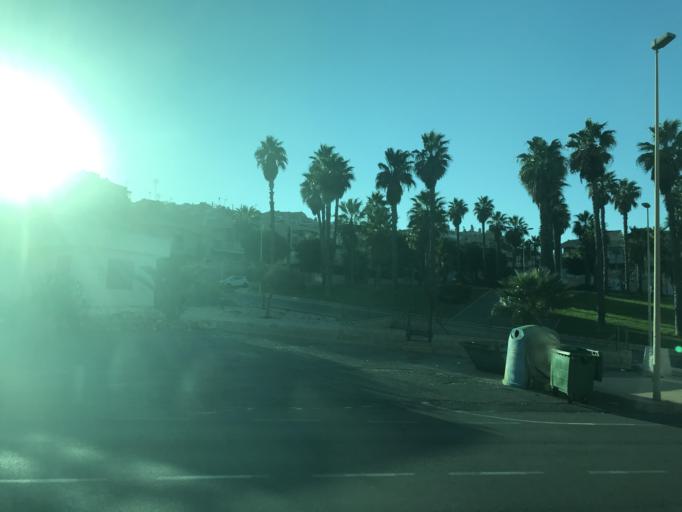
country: ES
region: Valencia
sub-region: Provincia de Alicante
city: Torrevieja
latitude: 38.0051
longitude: -0.6505
